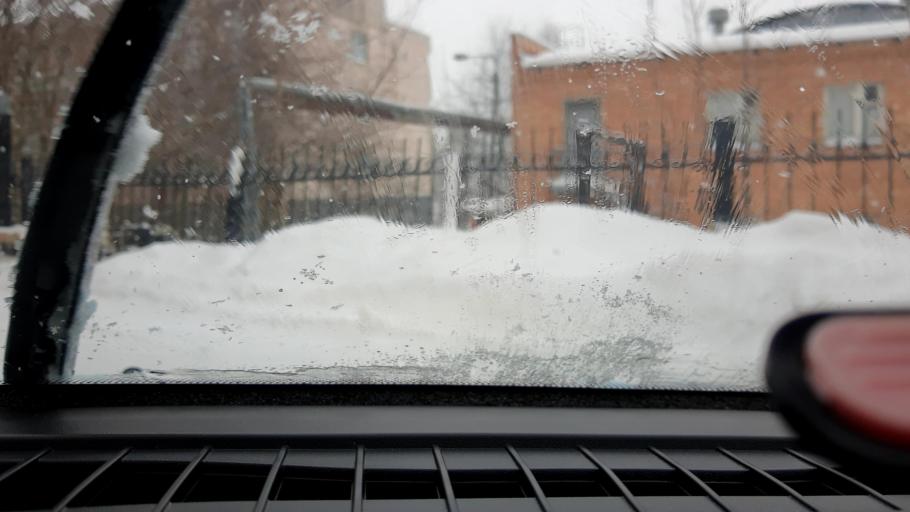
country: RU
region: Nizjnij Novgorod
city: Nizhniy Novgorod
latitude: 56.2358
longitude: 43.9435
